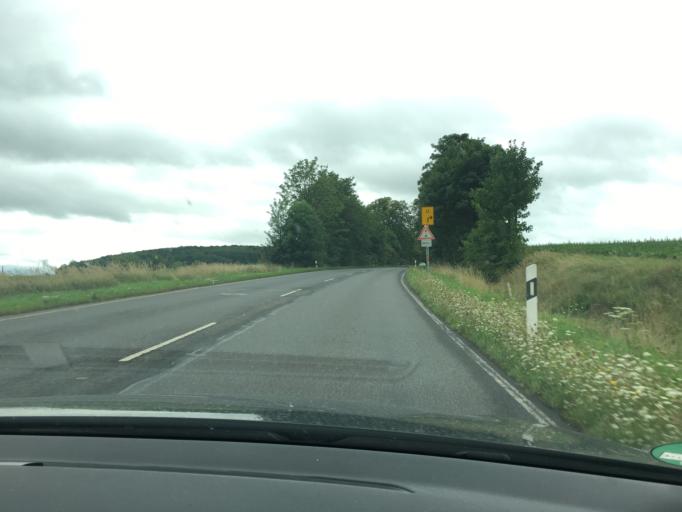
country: DE
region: North Rhine-Westphalia
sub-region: Regierungsbezirk Koln
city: Kreuzau
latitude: 50.7587
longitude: 6.4694
